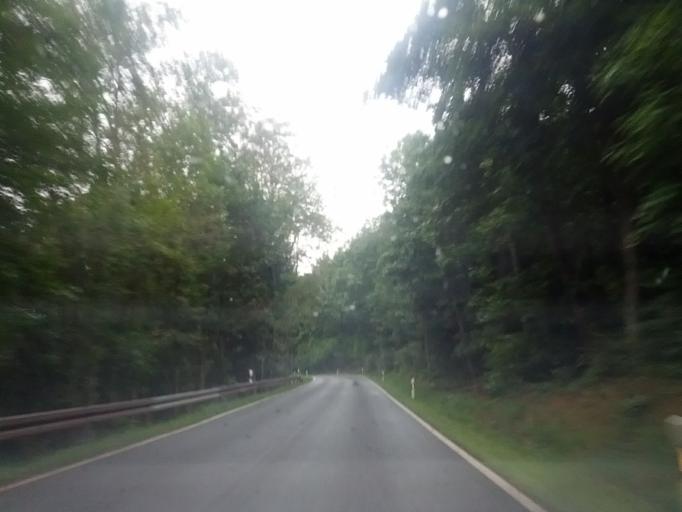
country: DE
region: Thuringia
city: Tabarz
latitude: 50.8948
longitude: 10.4877
